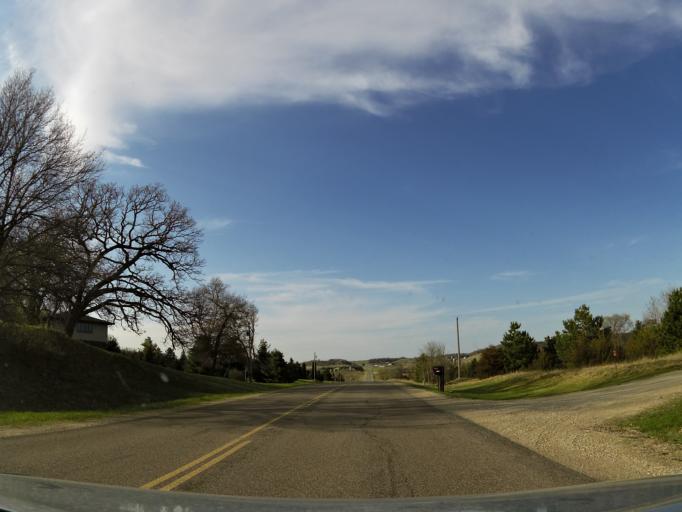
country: US
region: Wisconsin
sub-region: Pierce County
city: River Falls
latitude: 44.7572
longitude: -92.6396
